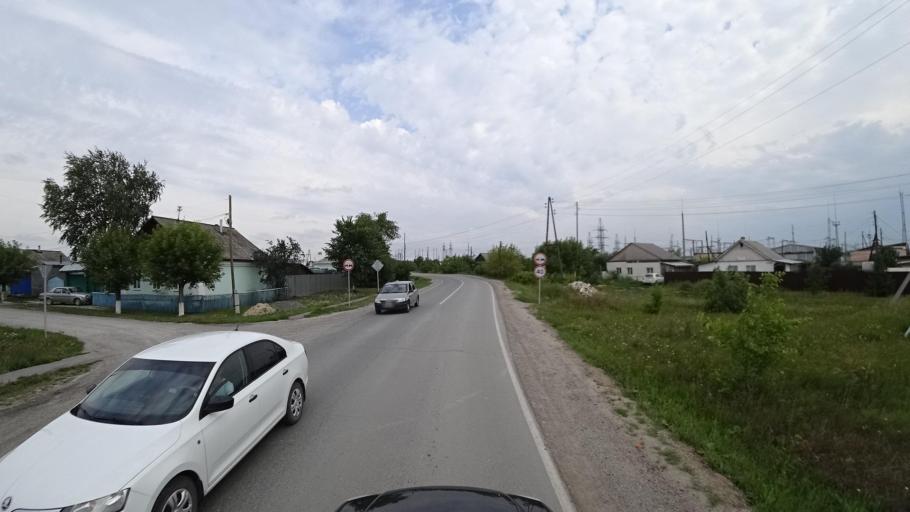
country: RU
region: Sverdlovsk
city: Kamyshlov
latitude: 56.8497
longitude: 62.7425
